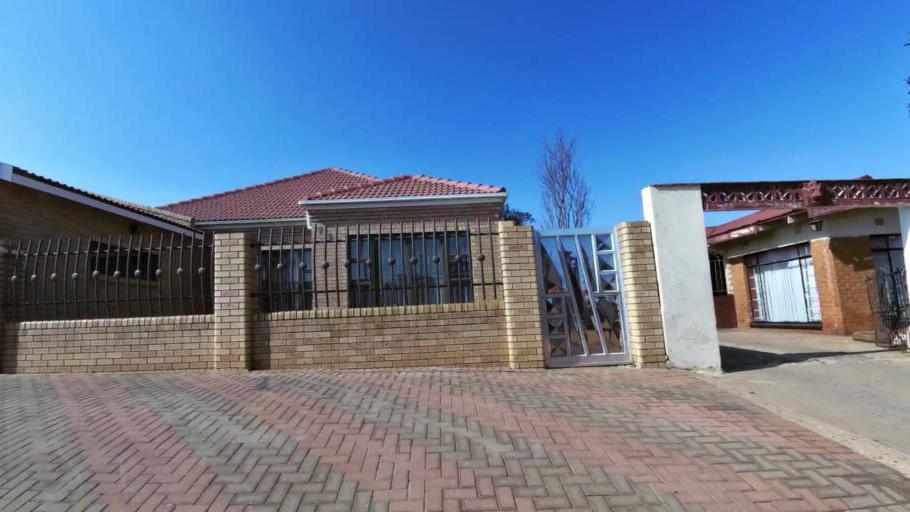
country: ZA
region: Gauteng
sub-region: City of Johannesburg Metropolitan Municipality
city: Soweto
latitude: -26.2445
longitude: 27.8933
